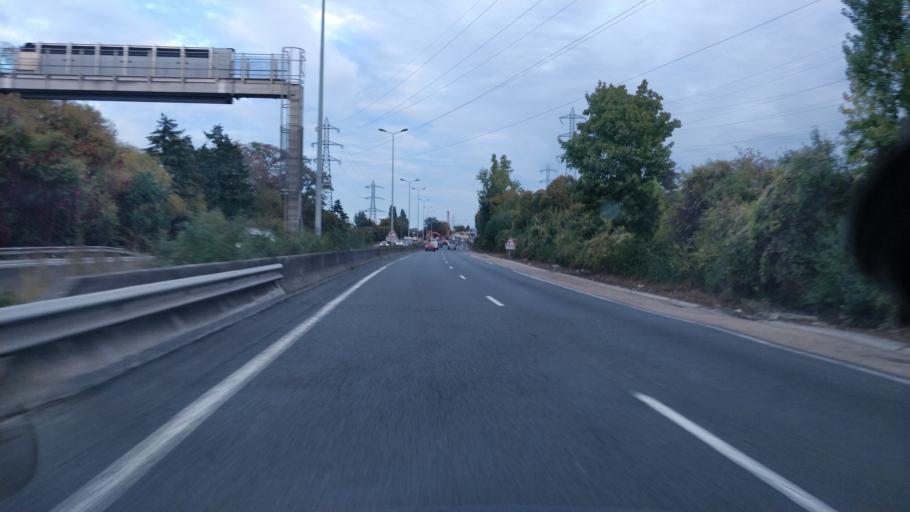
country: FR
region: Ile-de-France
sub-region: Departement de Seine-Saint-Denis
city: Villemomble
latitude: 48.8860
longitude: 2.4863
